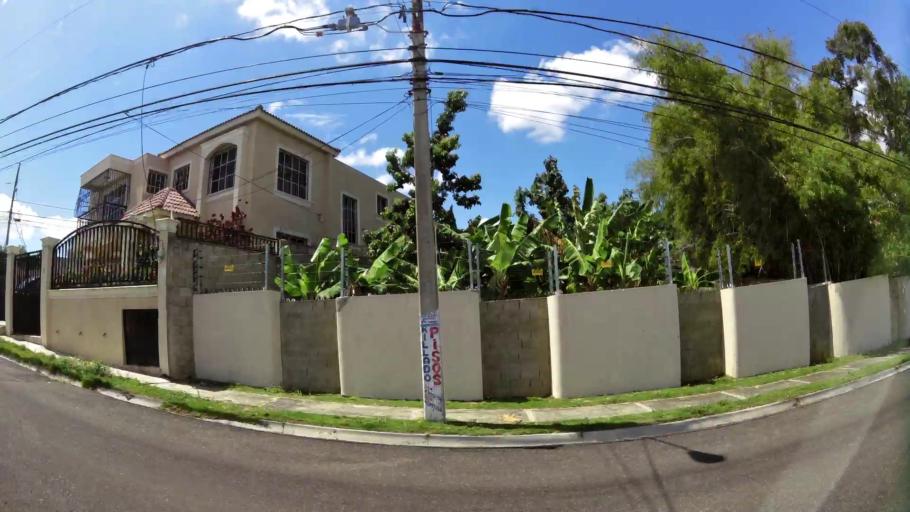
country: DO
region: Santiago
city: Santiago de los Caballeros
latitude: 19.4669
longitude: -70.6781
